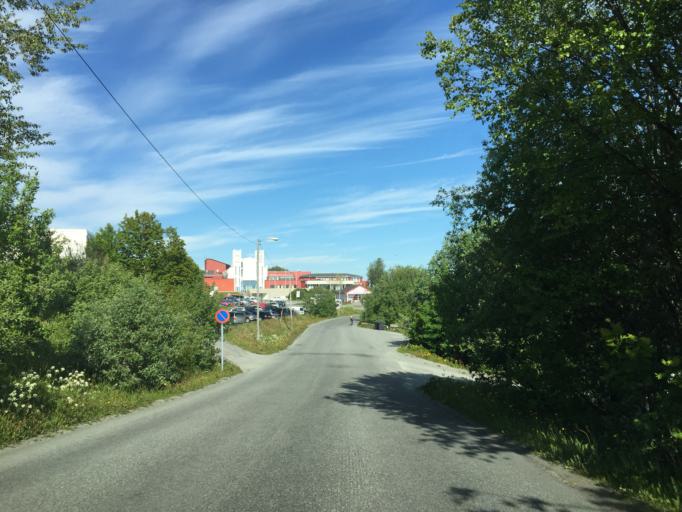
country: NO
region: Nordland
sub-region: Bodo
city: Lopsmarka
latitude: 67.2817
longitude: 14.5364
